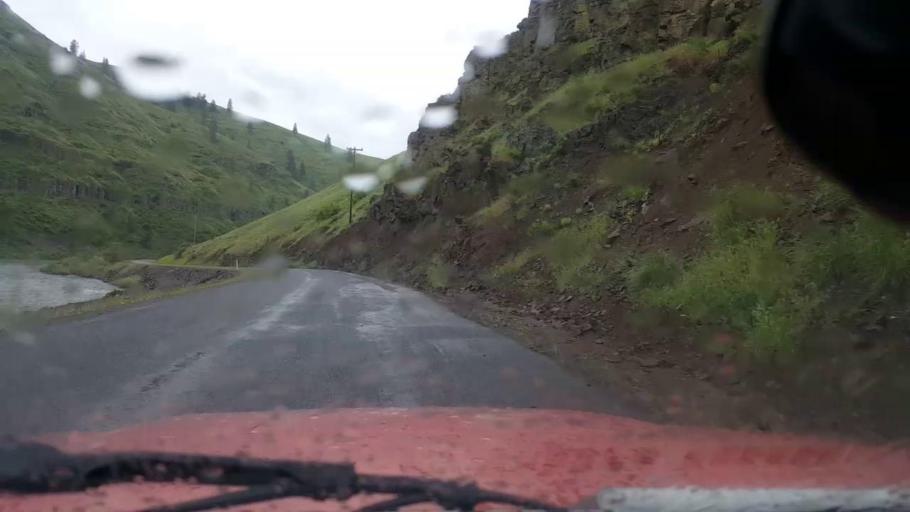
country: US
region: Washington
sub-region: Asotin County
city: Asotin
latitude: 46.0217
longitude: -117.3420
